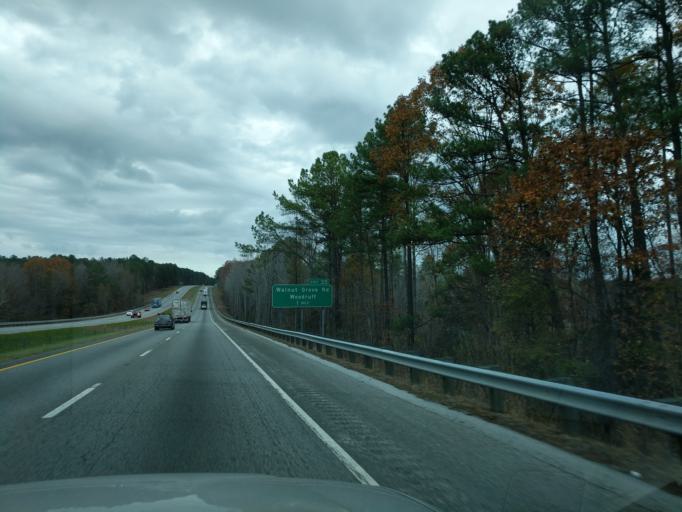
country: US
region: South Carolina
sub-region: Spartanburg County
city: Woodruff
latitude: 34.7307
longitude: -81.9509
